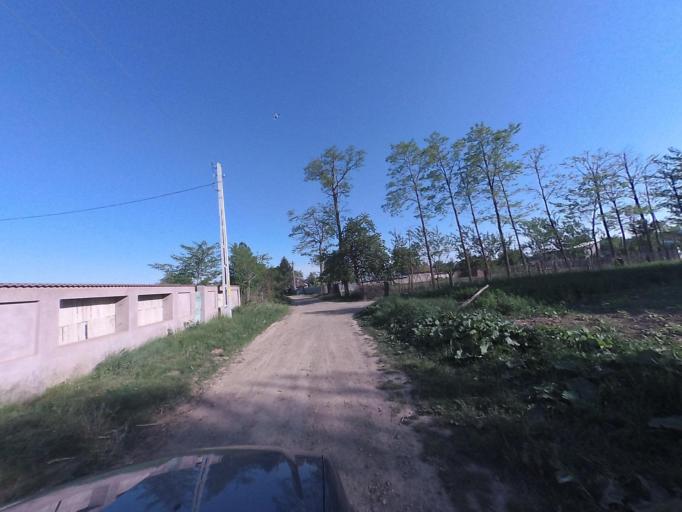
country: RO
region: Neamt
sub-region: Comuna Cordun
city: Pildesti
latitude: 46.9855
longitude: 26.8051
